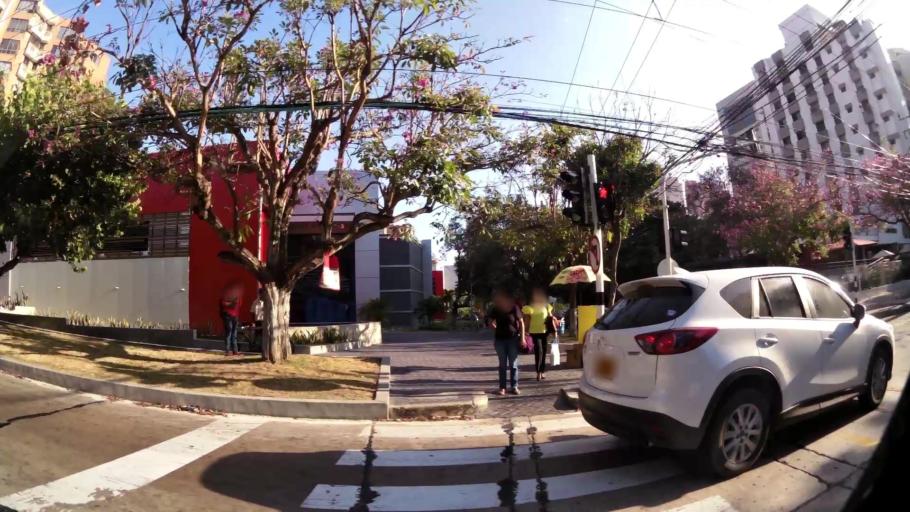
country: CO
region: Atlantico
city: Barranquilla
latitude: 11.0054
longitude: -74.8139
